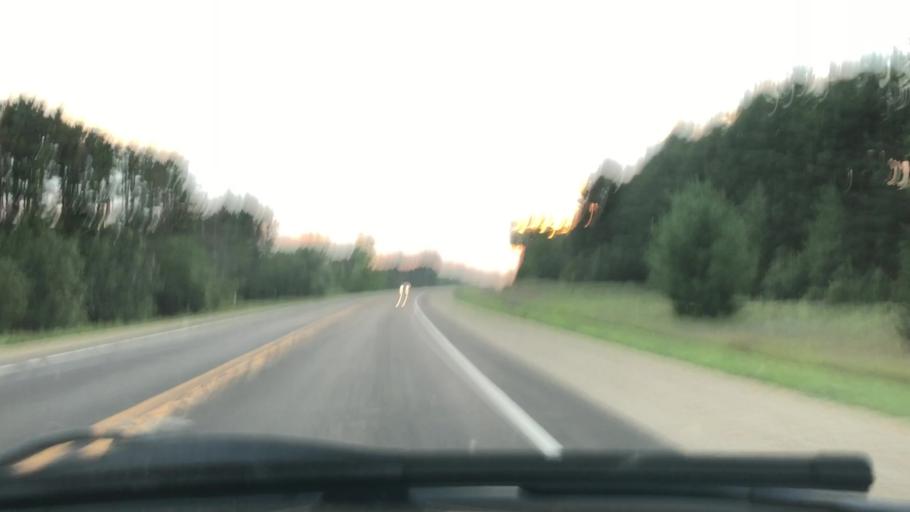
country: US
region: Wisconsin
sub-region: Sauk County
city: Spring Green
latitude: 43.1919
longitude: -90.2207
